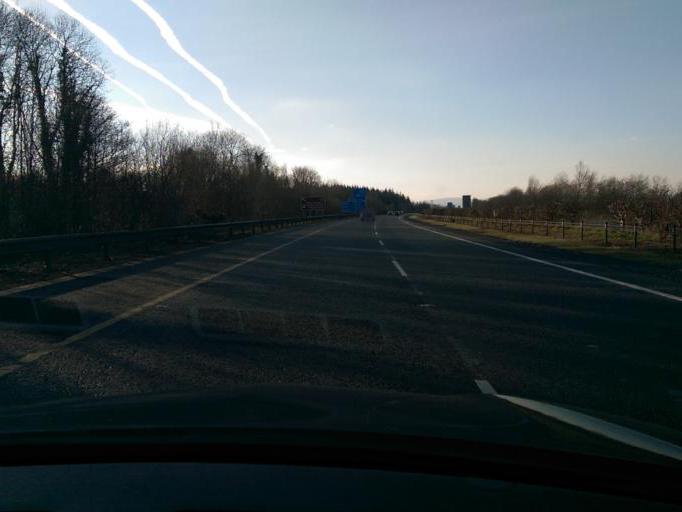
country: IE
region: Leinster
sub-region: Laois
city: Portlaoise
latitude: 53.0145
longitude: -7.3171
